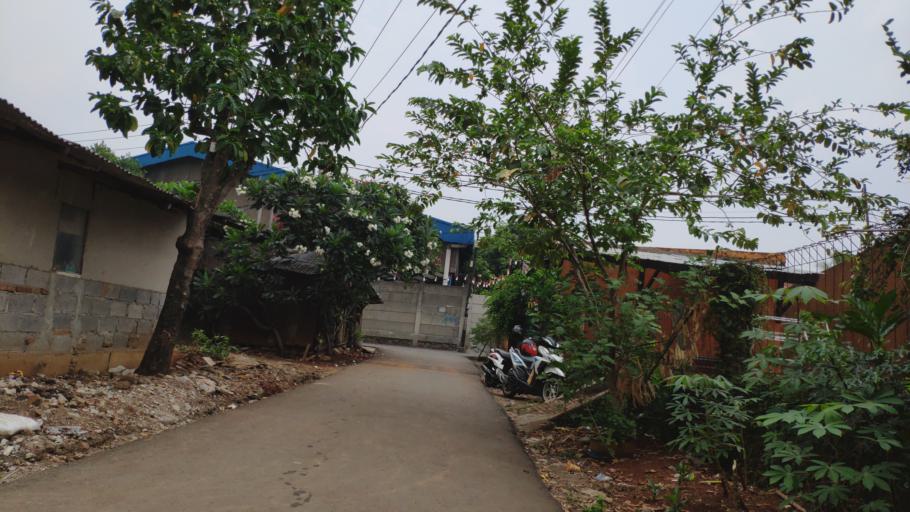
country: ID
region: Banten
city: South Tangerang
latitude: -6.2696
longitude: 106.7675
